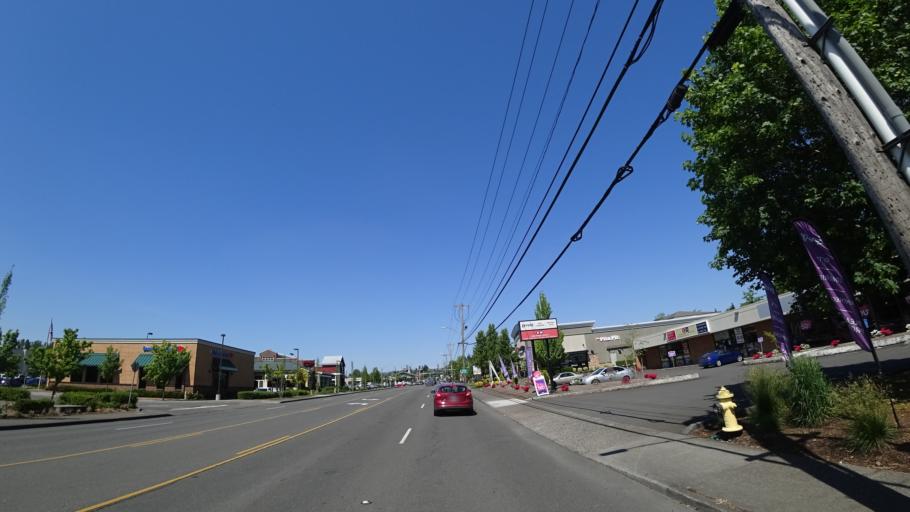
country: US
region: Oregon
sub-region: Washington County
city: Beaverton
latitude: 45.4957
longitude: -122.8092
